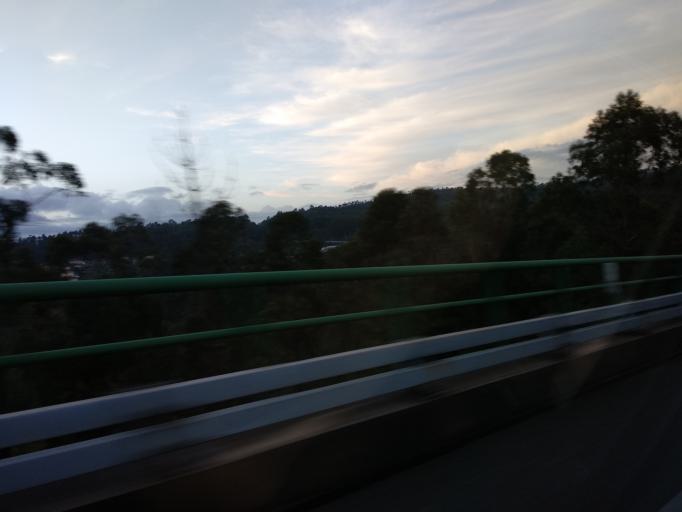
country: PT
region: Braga
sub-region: Braga
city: Oliveira
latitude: 41.4766
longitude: -8.4599
